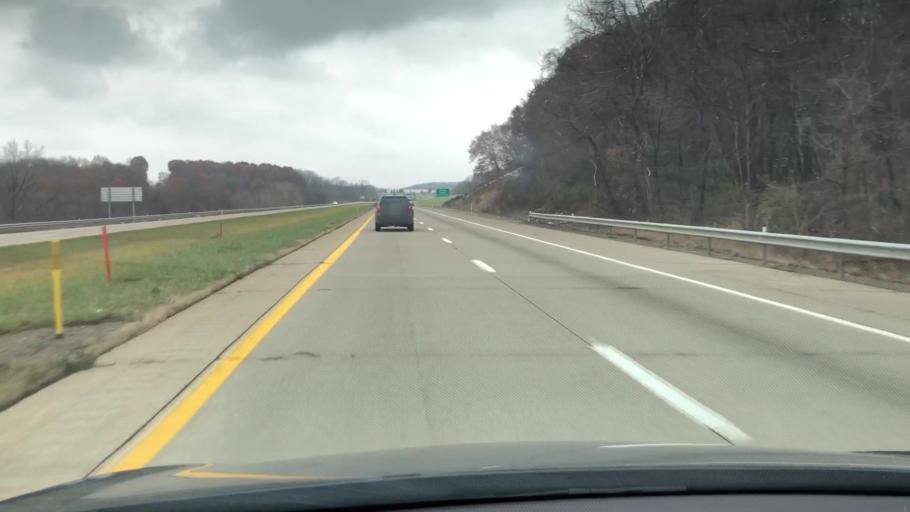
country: US
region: Pennsylvania
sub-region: Westmoreland County
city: New Stanton
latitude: 40.1995
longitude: -79.5779
